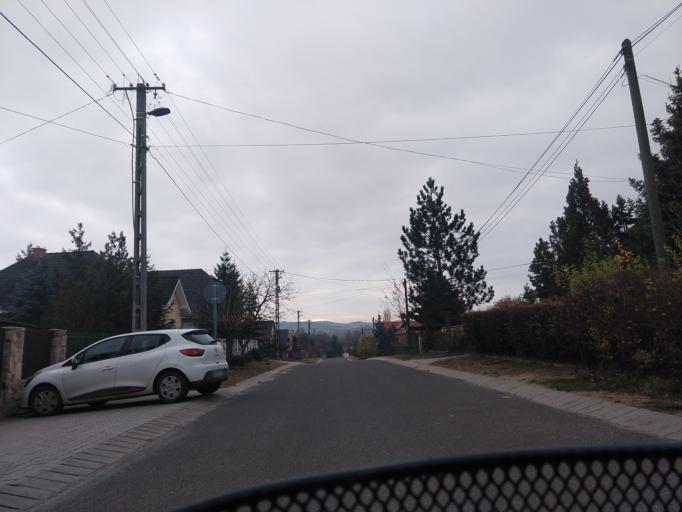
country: HU
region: Pest
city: Orbottyan
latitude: 47.6724
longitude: 19.2897
